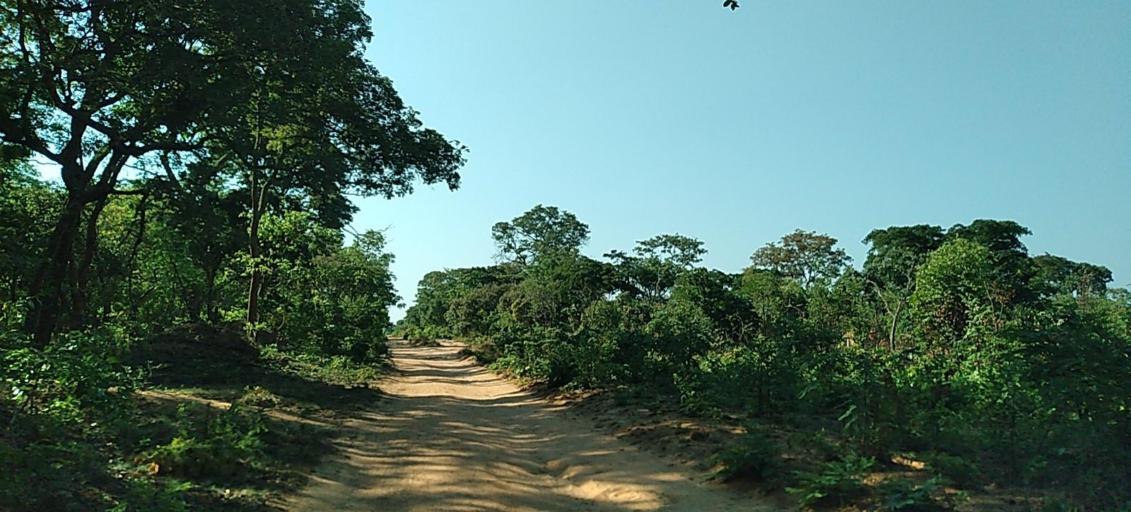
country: ZM
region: Central
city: Mkushi
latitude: -13.4613
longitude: 28.9121
